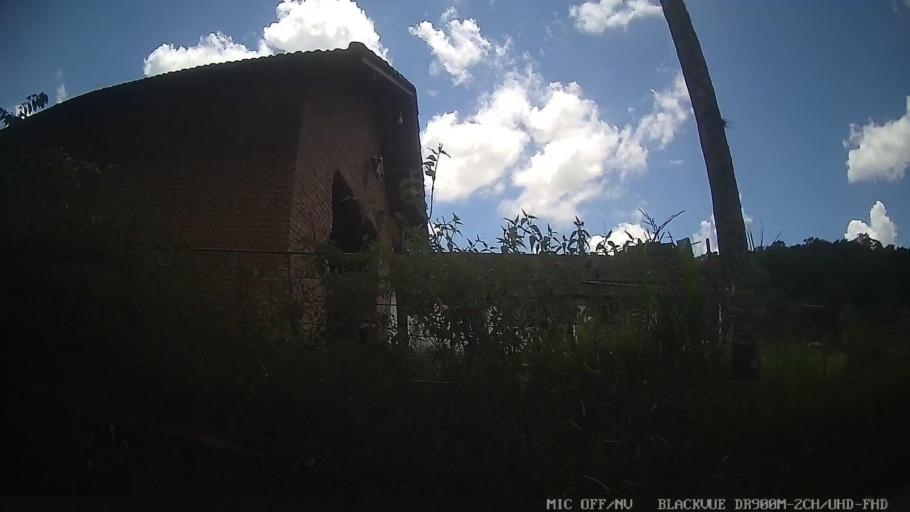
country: BR
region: Sao Paulo
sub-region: Braganca Paulista
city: Braganca Paulista
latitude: -23.0154
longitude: -46.4688
